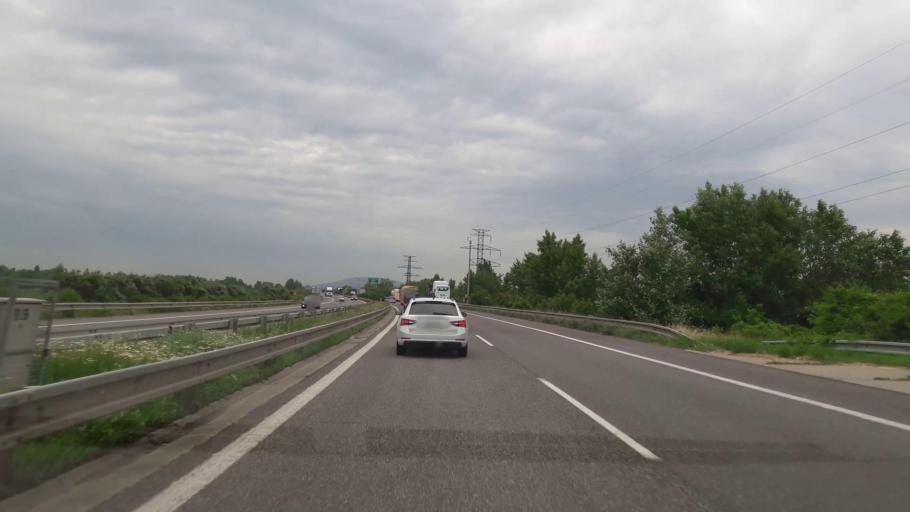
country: AT
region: Burgenland
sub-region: Politischer Bezirk Neusiedl am See
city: Kittsee
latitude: 48.1021
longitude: 17.0952
